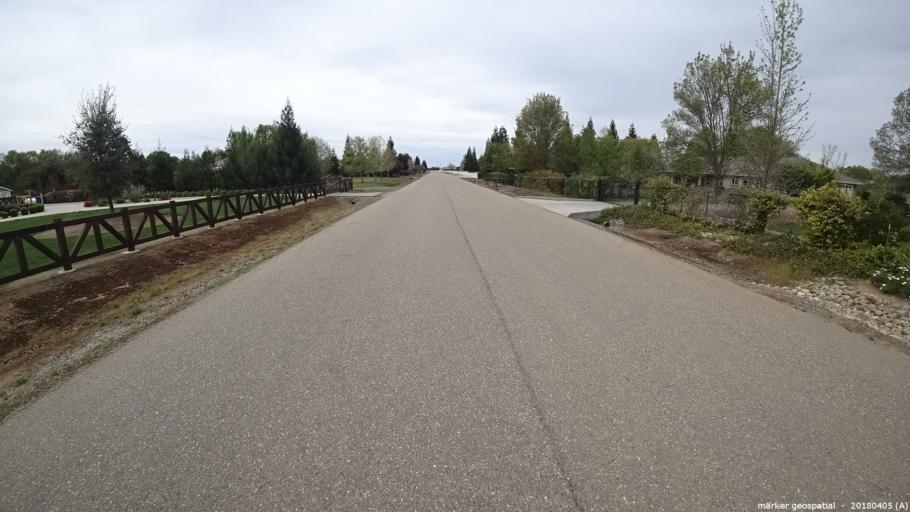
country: US
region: California
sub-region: Sacramento County
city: Galt
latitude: 38.2756
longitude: -121.3313
